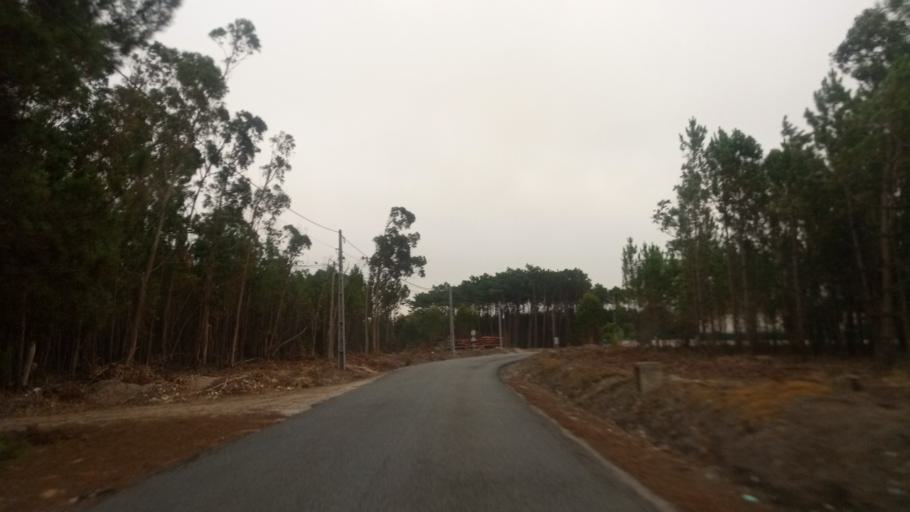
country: PT
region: Leiria
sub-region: Caldas da Rainha
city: Caldas da Rainha
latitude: 39.4466
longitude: -9.1694
